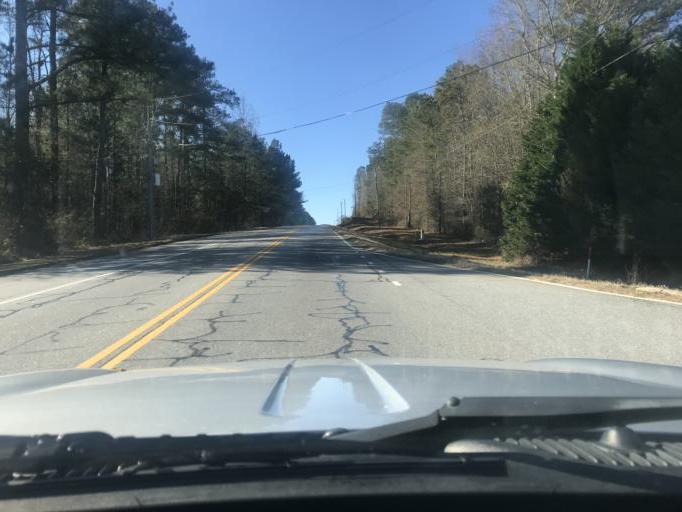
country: US
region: Georgia
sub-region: Barrow County
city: Winder
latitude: 33.9124
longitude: -83.7862
